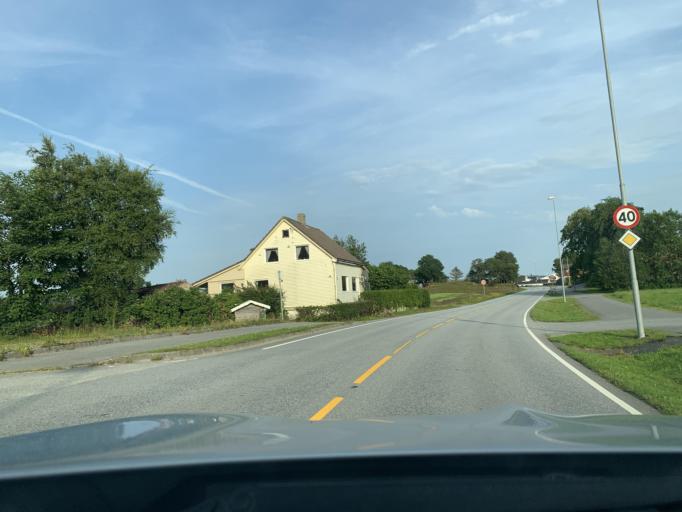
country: NO
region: Rogaland
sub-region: Time
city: Bryne
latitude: 58.7396
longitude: 5.6280
